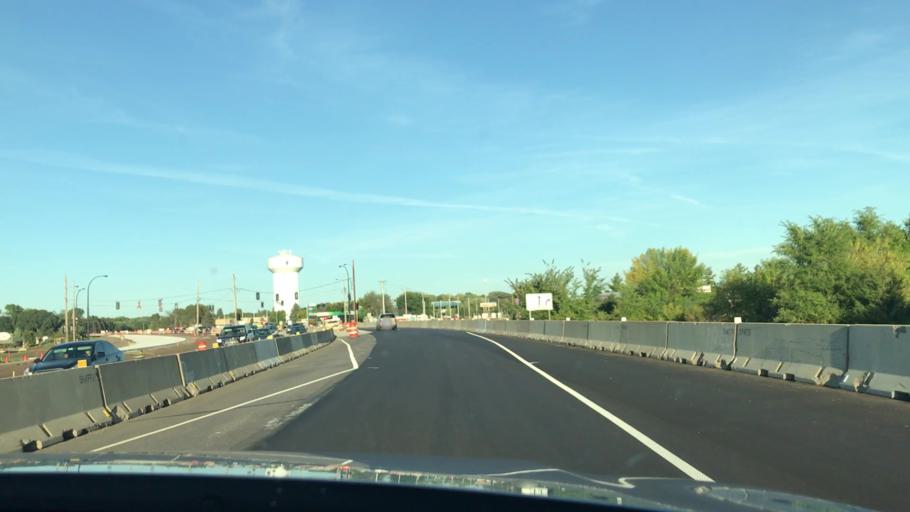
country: US
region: Minnesota
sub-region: Wright County
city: Otsego
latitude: 45.3060
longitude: -93.6112
